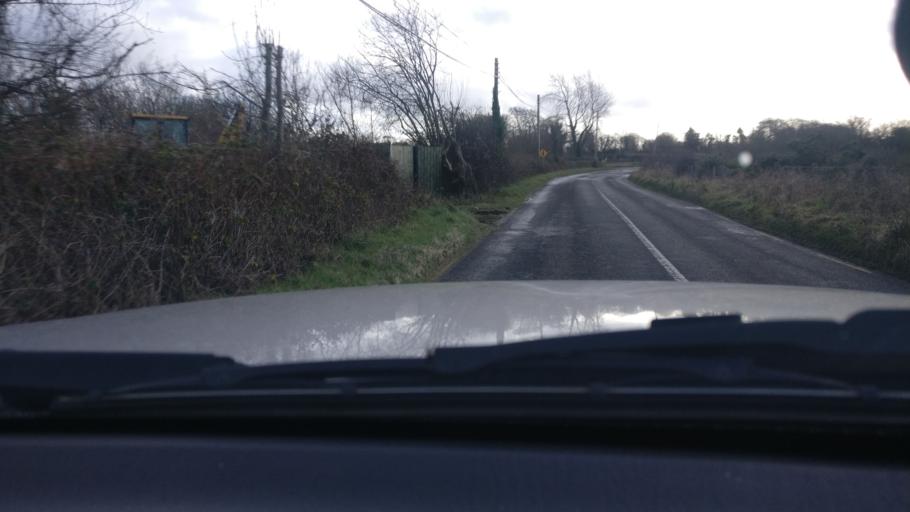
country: IE
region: Connaught
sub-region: County Galway
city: Ballinasloe
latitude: 53.2506
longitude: -8.2638
